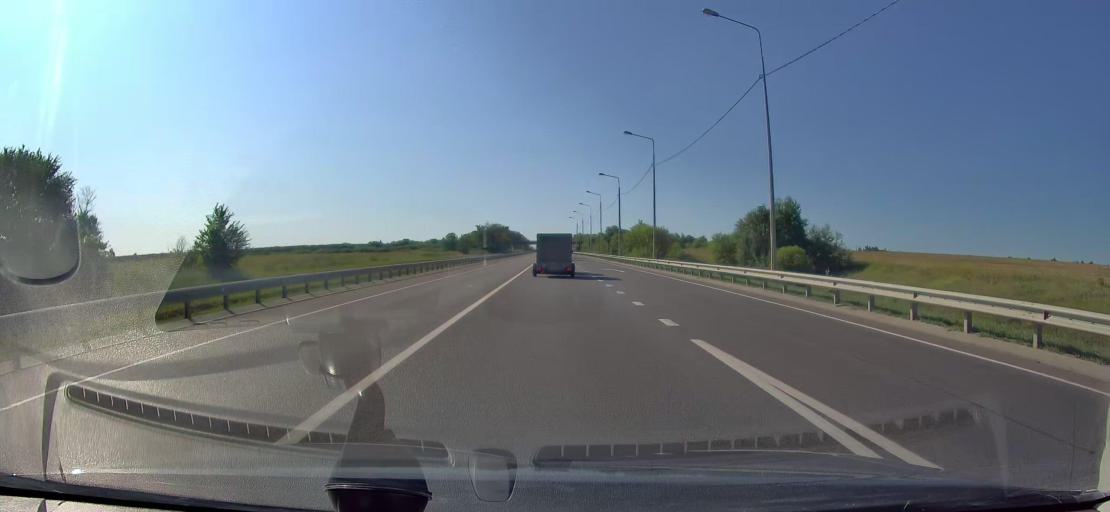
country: RU
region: Orjol
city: Kromy
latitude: 52.6386
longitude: 35.7493
